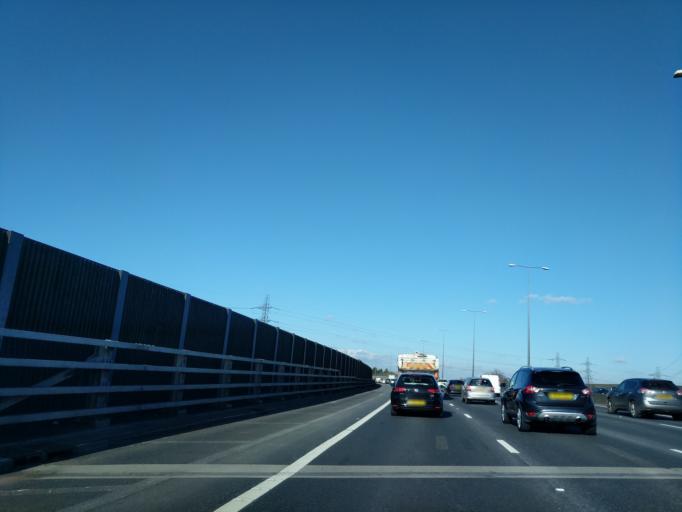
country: GB
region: England
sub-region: Surrey
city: Byfleet
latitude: 51.3474
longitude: -0.4858
